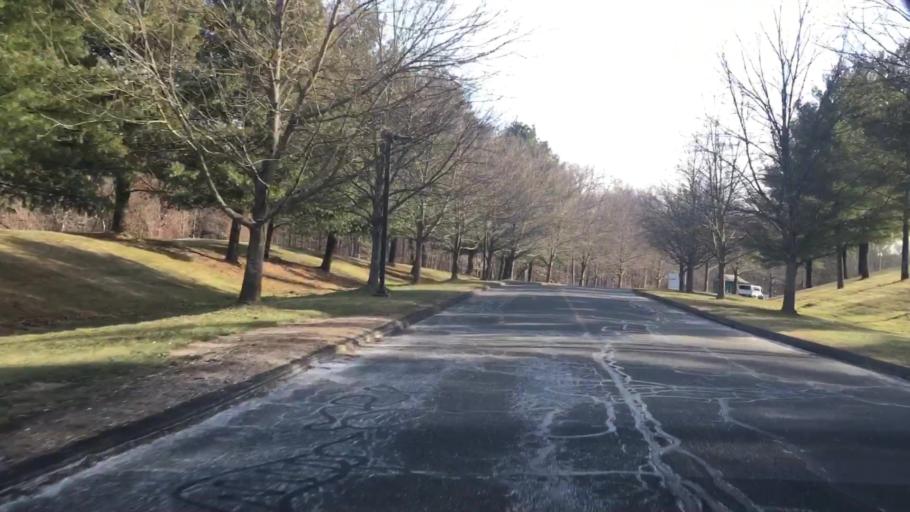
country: US
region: New York
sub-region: Putnam County
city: Peach Lake
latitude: 41.3749
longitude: -73.5259
